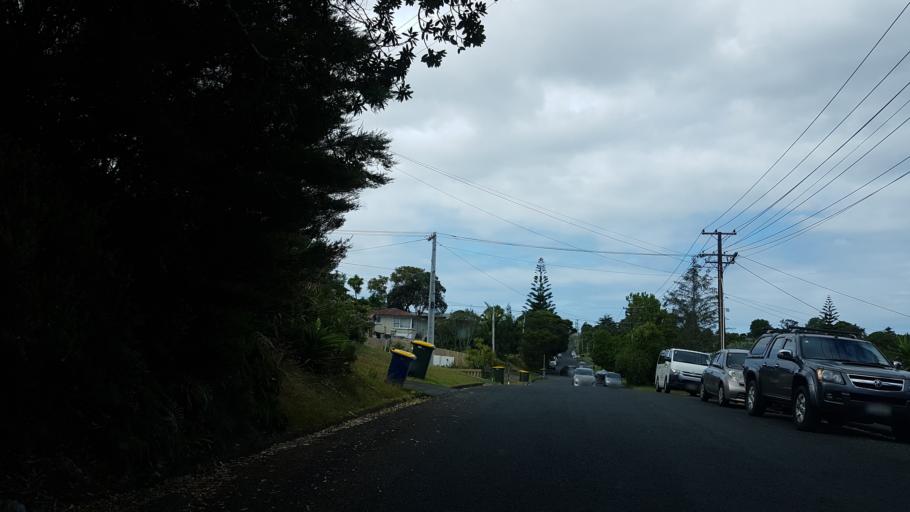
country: NZ
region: Auckland
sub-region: Auckland
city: North Shore
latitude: -36.7728
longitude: 174.7234
